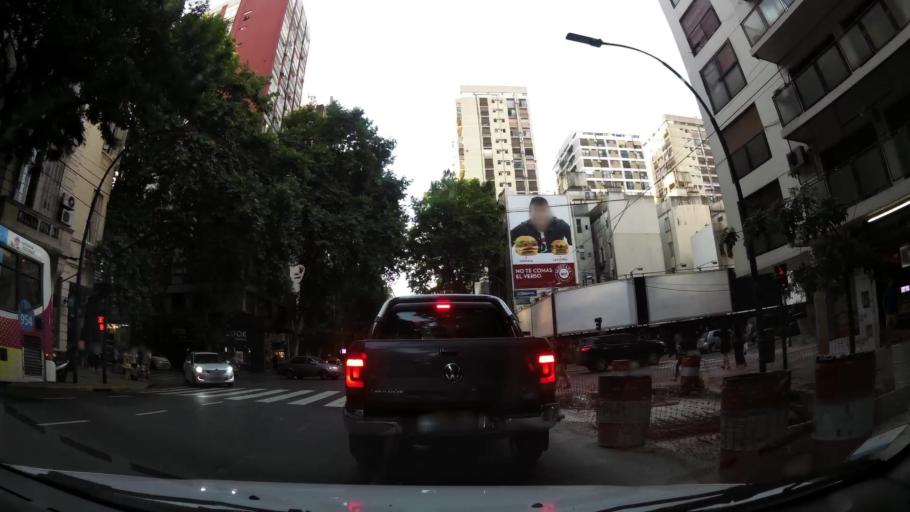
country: AR
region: Buenos Aires F.D.
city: Retiro
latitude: -34.5859
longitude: -58.4148
